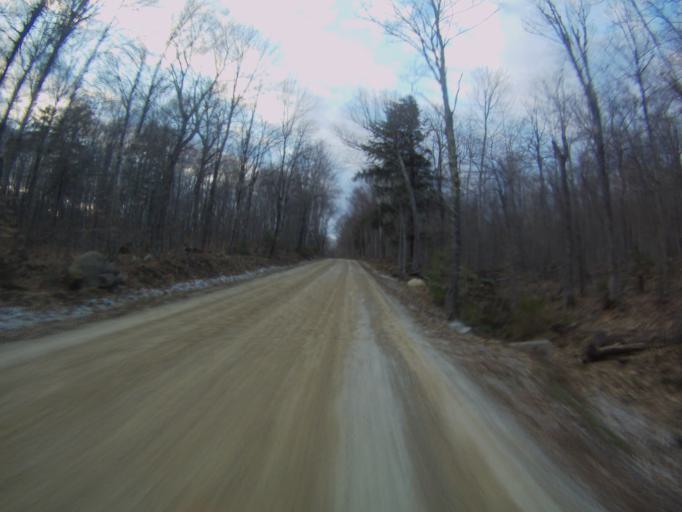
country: US
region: Vermont
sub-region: Rutland County
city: Brandon
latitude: 43.9216
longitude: -73.0186
